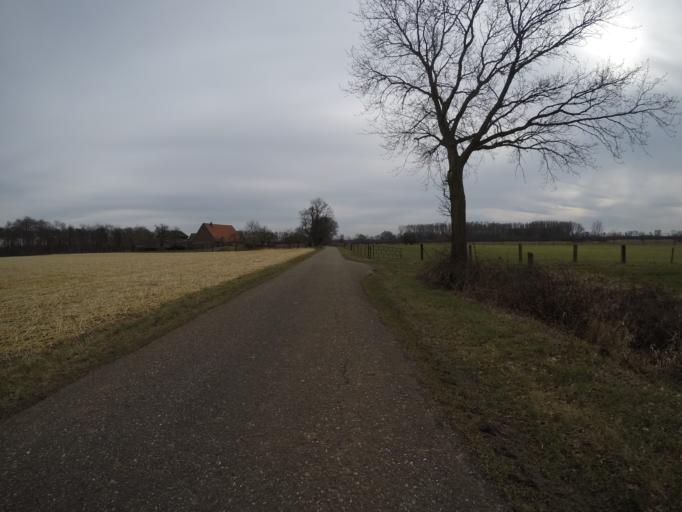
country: DE
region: North Rhine-Westphalia
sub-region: Regierungsbezirk Dusseldorf
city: Hamminkeln
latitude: 51.7542
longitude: 6.6024
